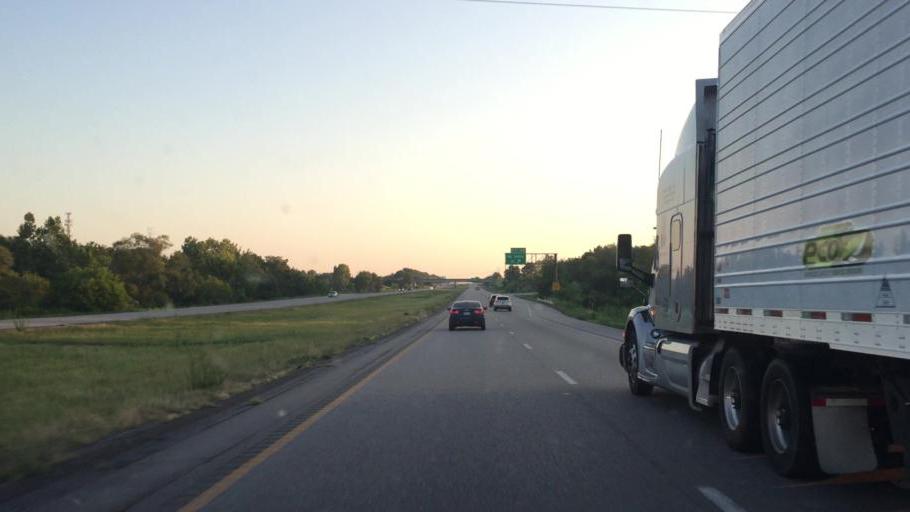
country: US
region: Missouri
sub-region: Clay County
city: Pleasant Valley
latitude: 39.2813
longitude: -94.5101
